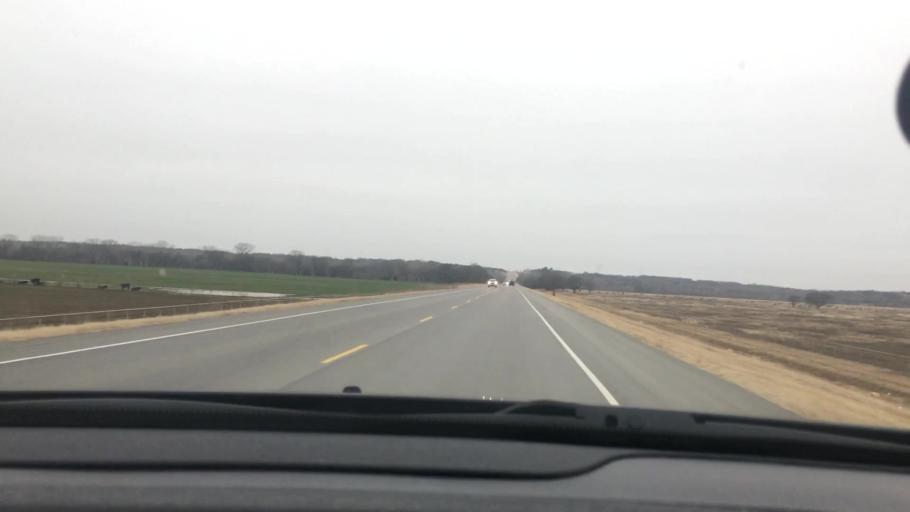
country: US
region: Oklahoma
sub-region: Garvin County
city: Wynnewood
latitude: 34.6227
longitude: -97.1842
